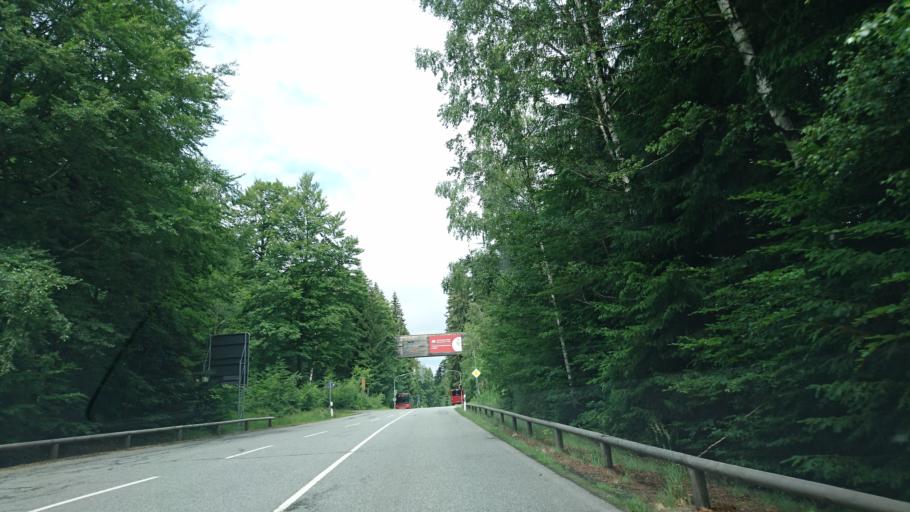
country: DE
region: Bavaria
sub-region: Lower Bavaria
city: Neuschonau
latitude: 48.8914
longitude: 13.4892
